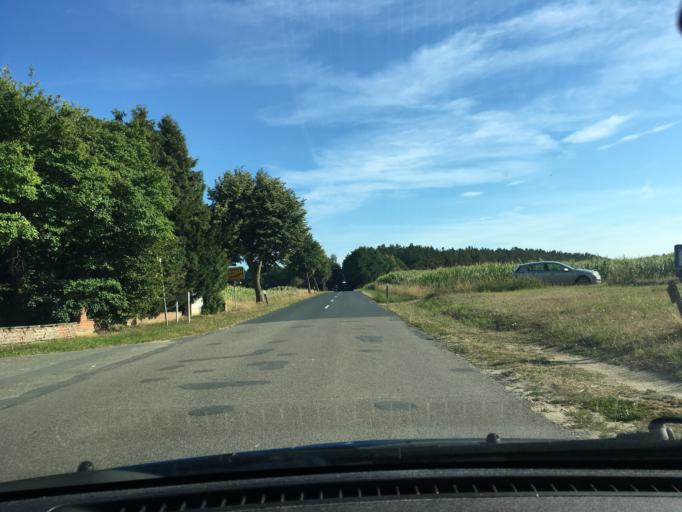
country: DE
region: Lower Saxony
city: Thomasburg
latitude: 53.2204
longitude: 10.7032
